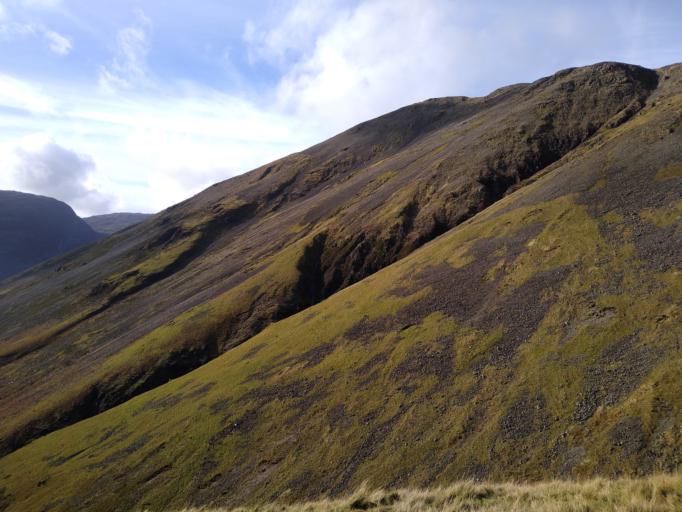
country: GB
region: England
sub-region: Cumbria
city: Keswick
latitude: 54.4782
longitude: -3.2304
